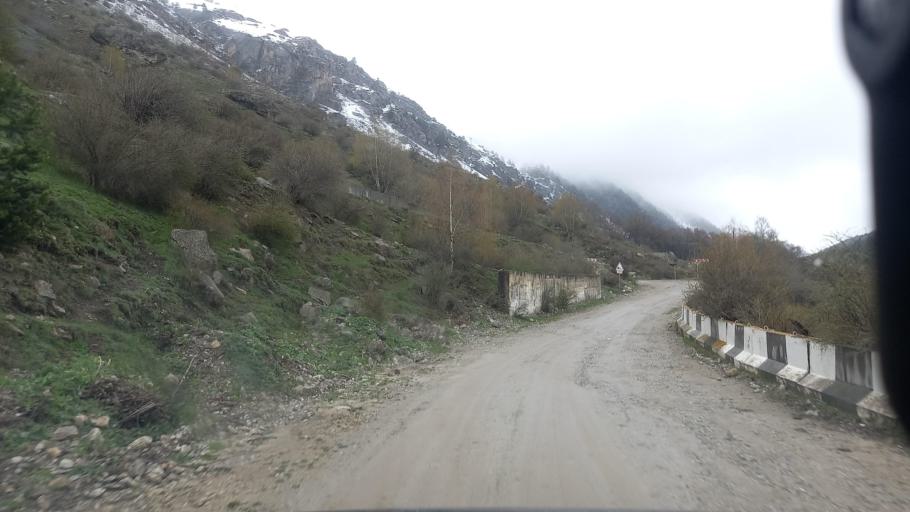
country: RU
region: Kabardino-Balkariya
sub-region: El'brusskiy Rayon
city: El'brus
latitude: 43.2262
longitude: 42.6632
